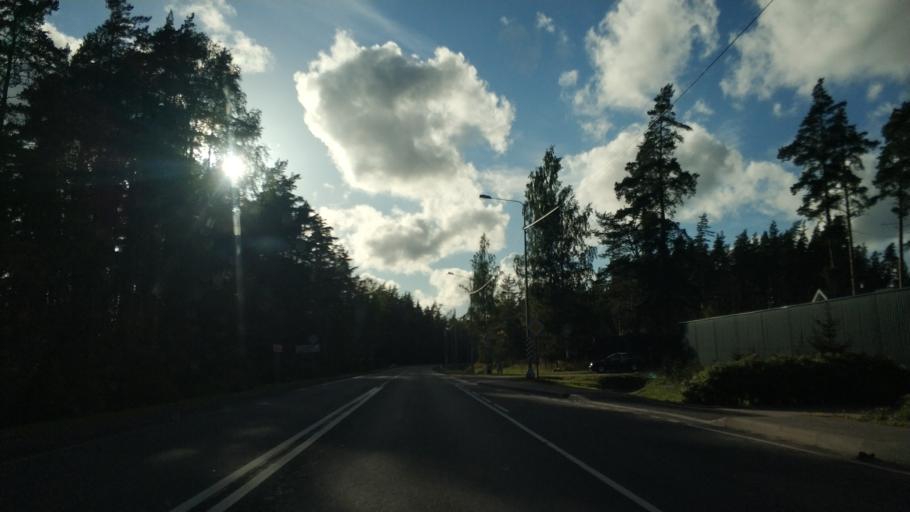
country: RU
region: Leningrad
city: Sapernoye
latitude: 60.7134
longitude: 30.0217
